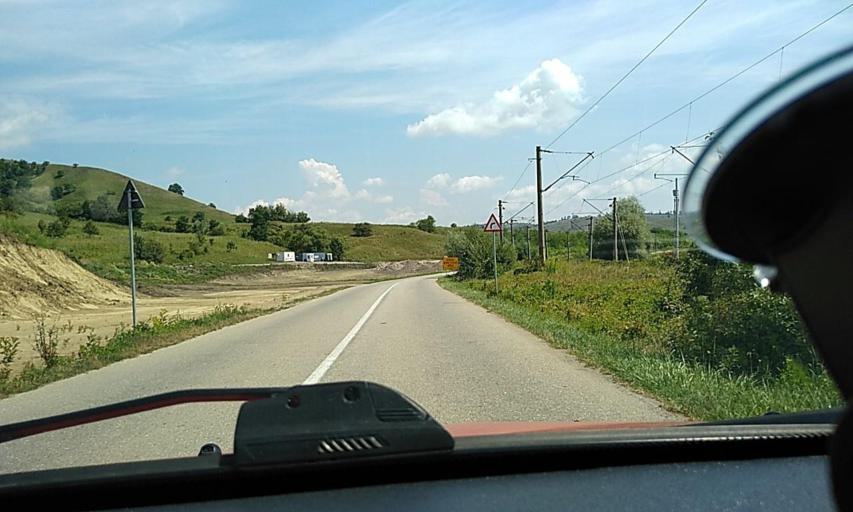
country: RO
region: Brasov
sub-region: Comuna Hoghiz
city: Hoghiz
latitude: 46.0289
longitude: 25.3639
